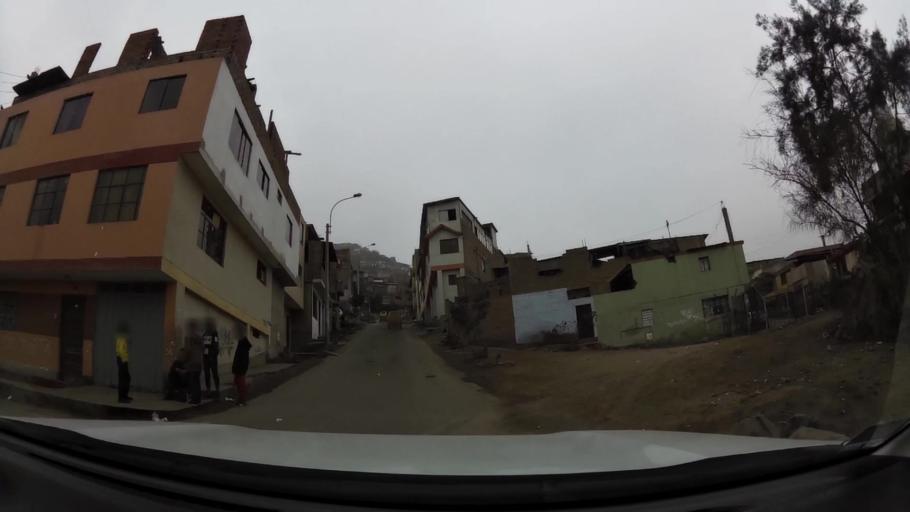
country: PE
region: Lima
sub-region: Lima
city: Surco
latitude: -12.1545
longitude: -76.9610
